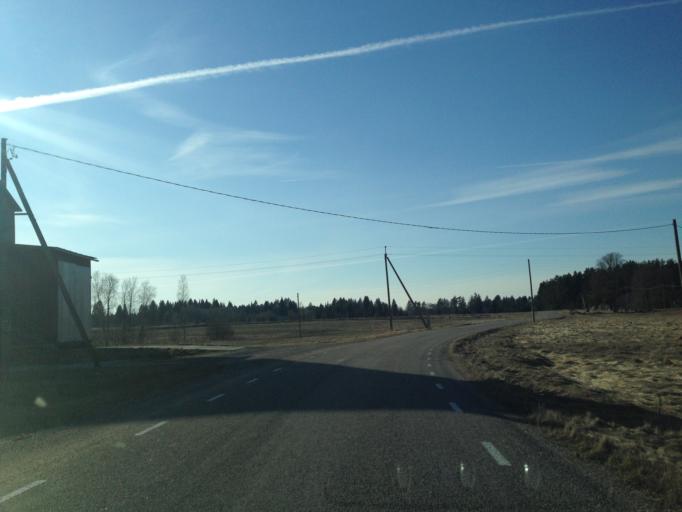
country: EE
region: Harju
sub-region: Nissi vald
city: Turba
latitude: 59.1388
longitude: 24.1685
